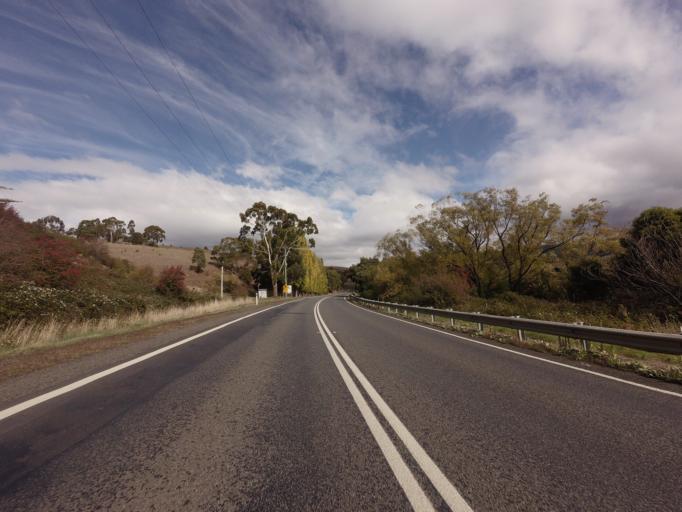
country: AU
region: Tasmania
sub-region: Derwent Valley
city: New Norfolk
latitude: -42.7298
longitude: 146.9568
